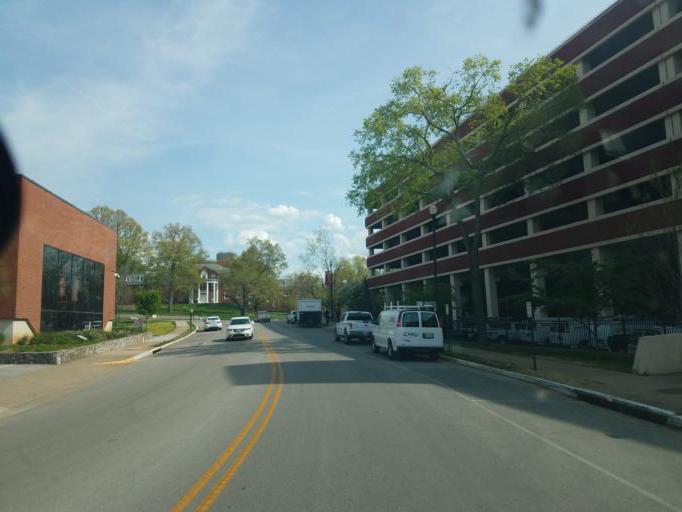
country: US
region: Kentucky
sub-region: Warren County
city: Bowling Green
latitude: 36.9873
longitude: -86.4563
